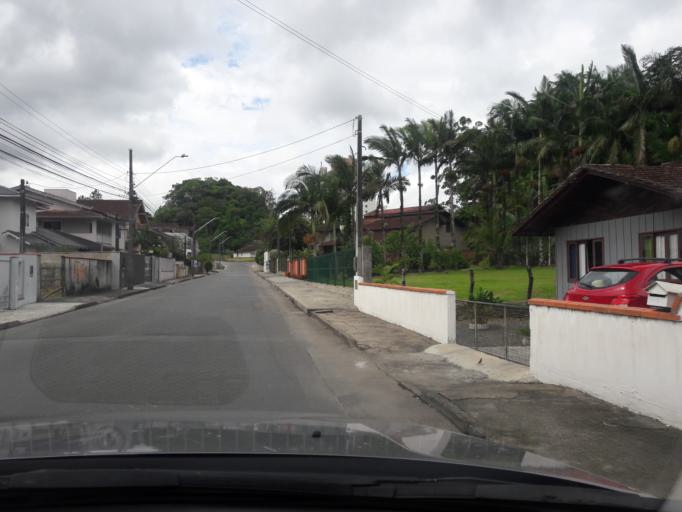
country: BR
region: Santa Catarina
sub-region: Joinville
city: Joinville
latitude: -26.3231
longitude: -48.8652
